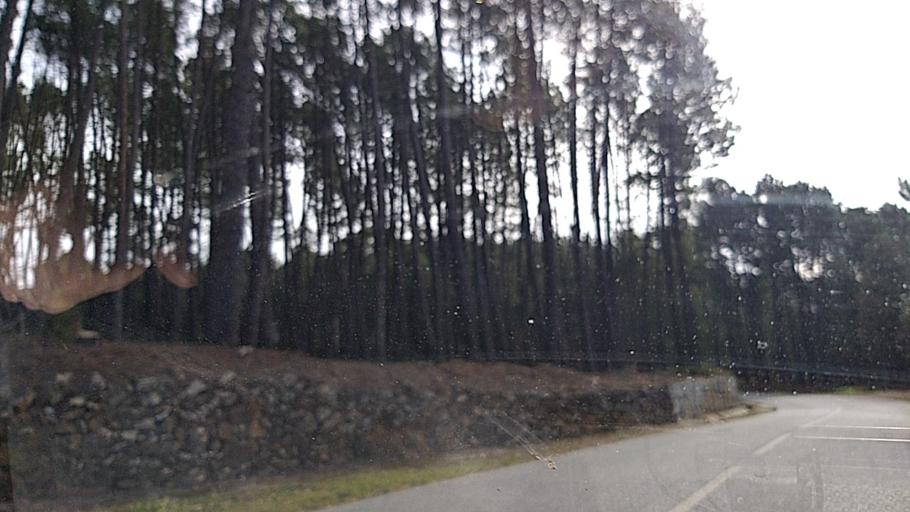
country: PT
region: Guarda
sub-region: Fornos de Algodres
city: Fornos de Algodres
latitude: 40.6891
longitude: -7.5453
